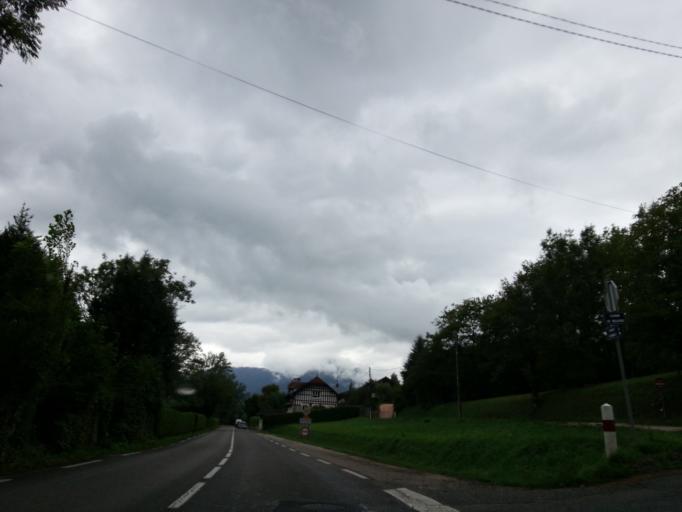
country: FR
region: Rhone-Alpes
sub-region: Departement de la Haute-Savoie
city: Talloires
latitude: 45.8197
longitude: 6.2068
